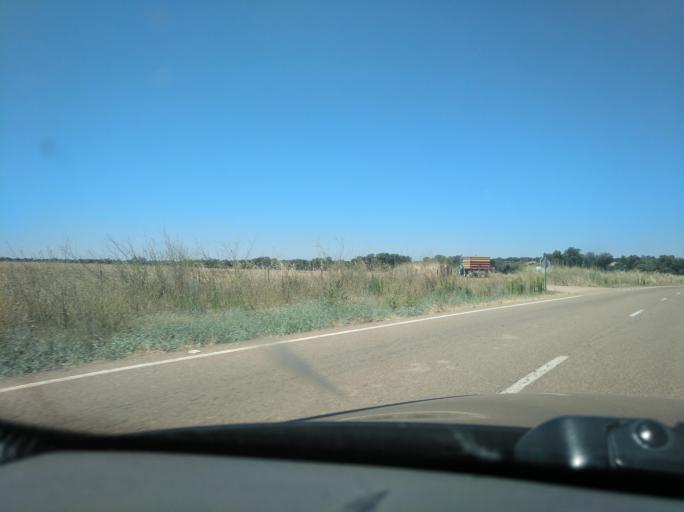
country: ES
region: Extremadura
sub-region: Provincia de Badajoz
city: Olivenza
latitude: 38.7067
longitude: -7.1784
